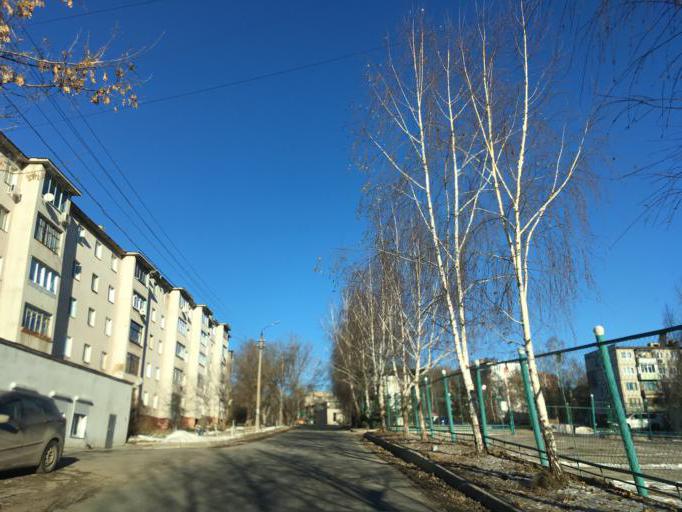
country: RU
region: Tula
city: Tula
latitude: 54.1927
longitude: 37.6763
